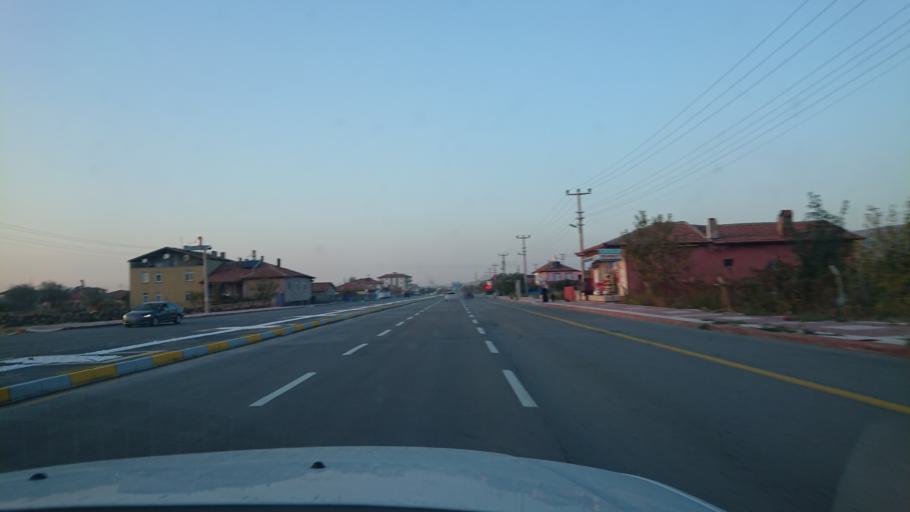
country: TR
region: Aksaray
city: Aksaray
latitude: 38.3396
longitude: 34.0472
